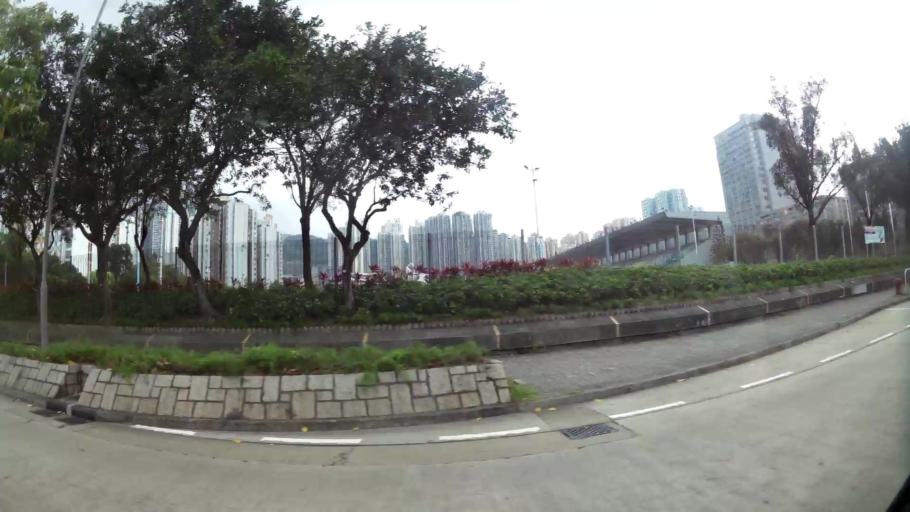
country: HK
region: Kowloon City
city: Kowloon
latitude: 22.3270
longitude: 114.2085
